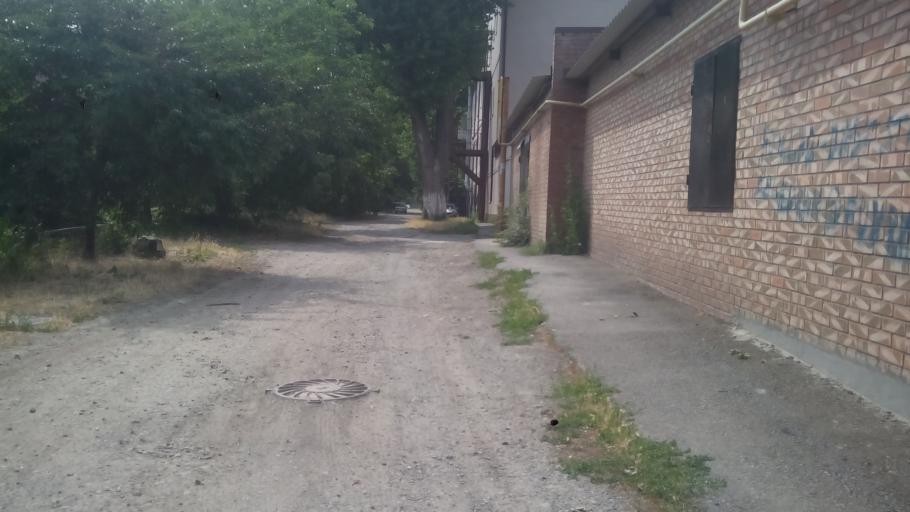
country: RU
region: Rostov
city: Rostov-na-Donu
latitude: 47.2156
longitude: 39.6705
